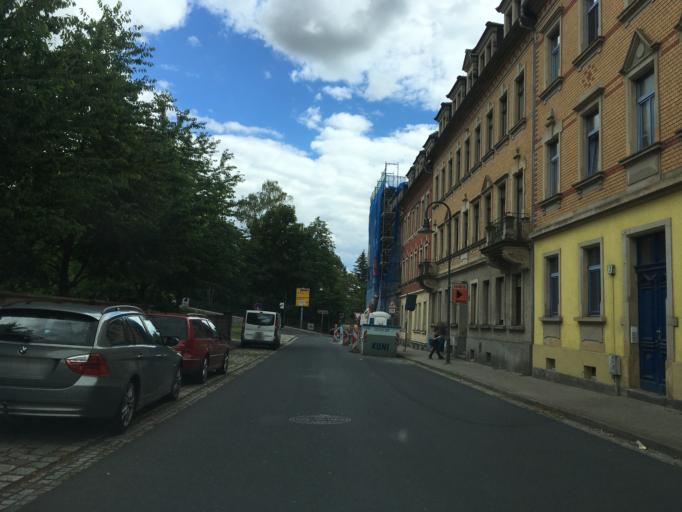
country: DE
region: Saxony
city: Radeberg
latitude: 51.1190
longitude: 13.9182
